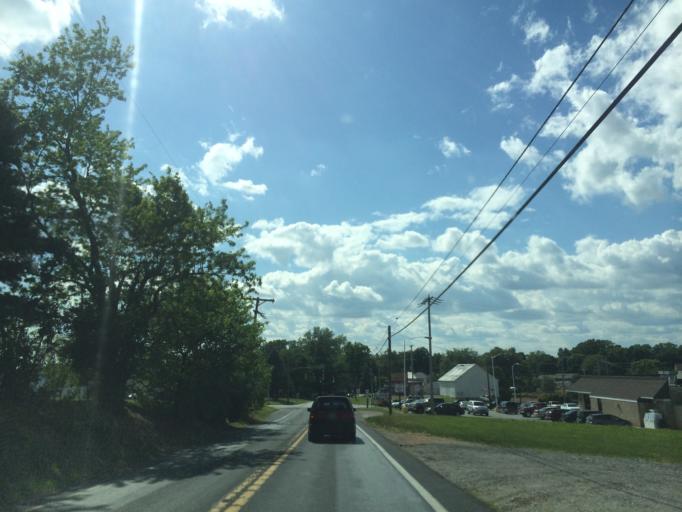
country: US
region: Pennsylvania
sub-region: York County
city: Parkville
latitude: 39.7948
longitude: -76.9429
